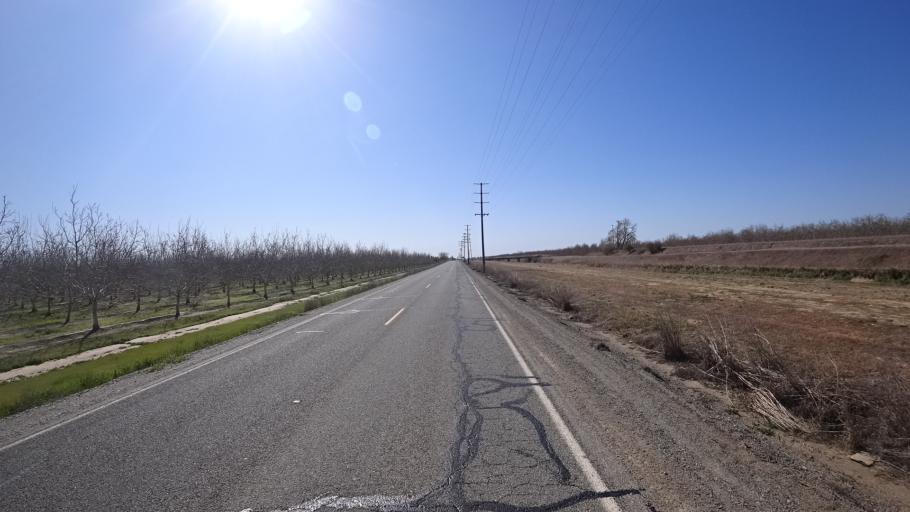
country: US
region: California
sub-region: Glenn County
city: Hamilton City
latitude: 39.7585
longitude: -122.0262
